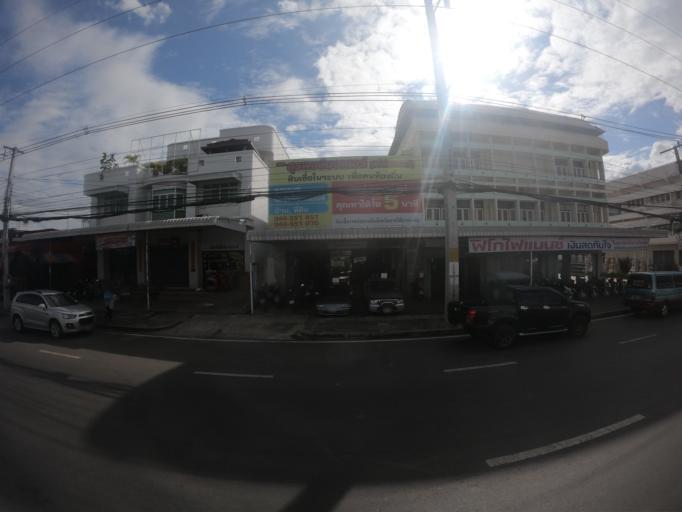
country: TH
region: Surin
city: Prasat
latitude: 14.6324
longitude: 103.4078
